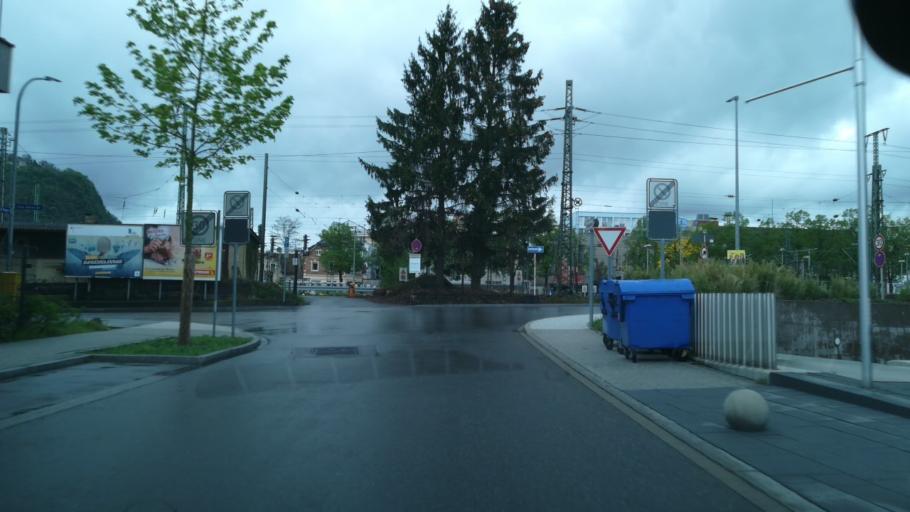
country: DE
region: Baden-Wuerttemberg
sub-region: Freiburg Region
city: Singen
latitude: 47.7570
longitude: 8.8392
